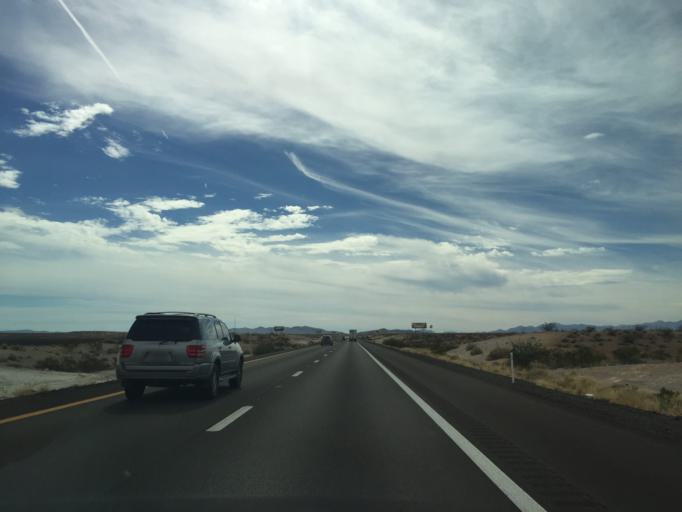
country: US
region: Nevada
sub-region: Clark County
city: Moapa Town
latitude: 36.5347
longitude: -114.7203
